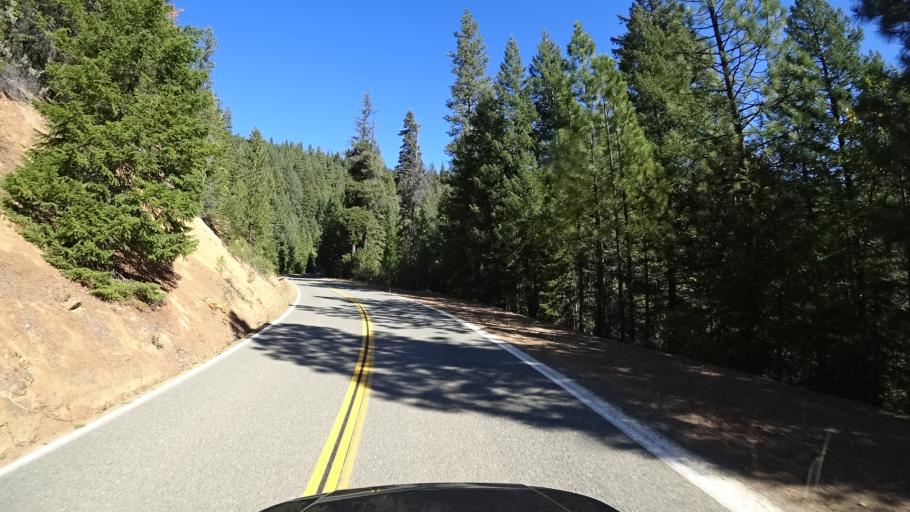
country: US
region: California
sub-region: Trinity County
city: Weaverville
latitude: 41.2201
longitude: -123.0221
